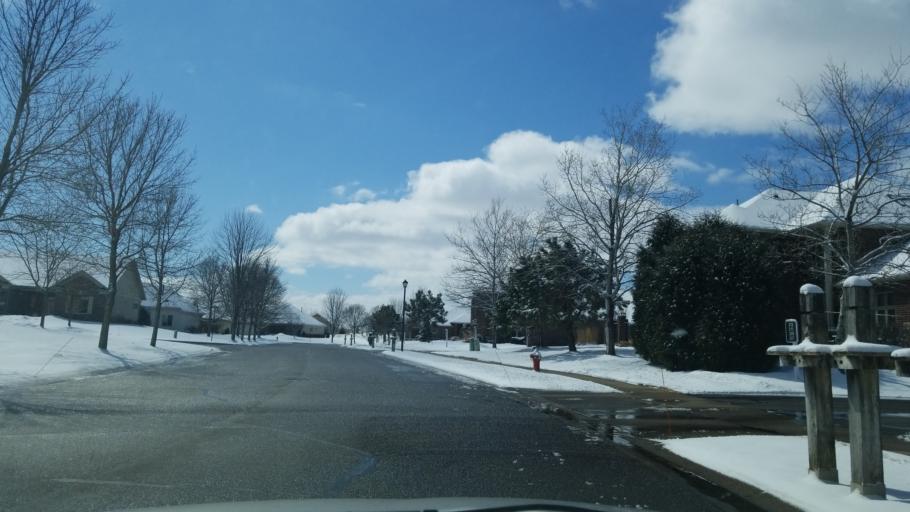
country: US
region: Wisconsin
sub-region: Saint Croix County
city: Hudson
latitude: 44.9568
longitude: -92.7084
